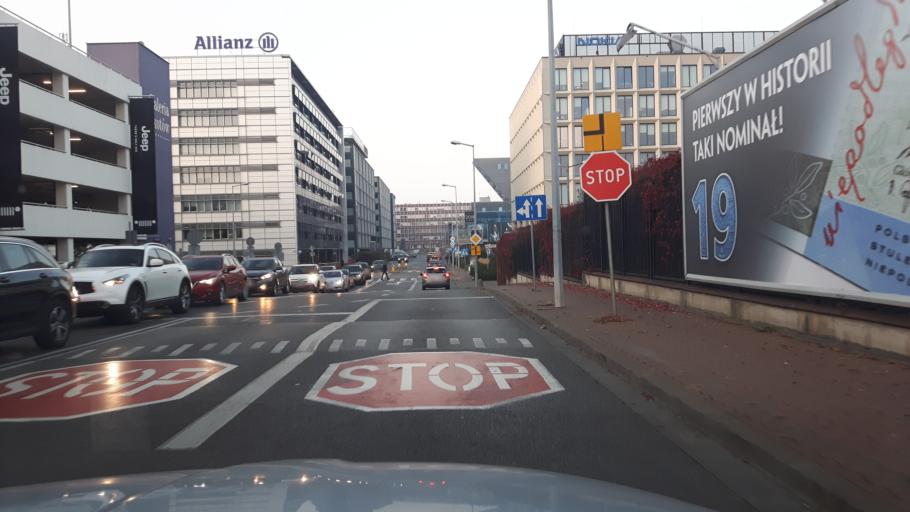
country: PL
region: Masovian Voivodeship
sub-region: Warszawa
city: Mokotow
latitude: 52.1803
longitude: 21.0061
